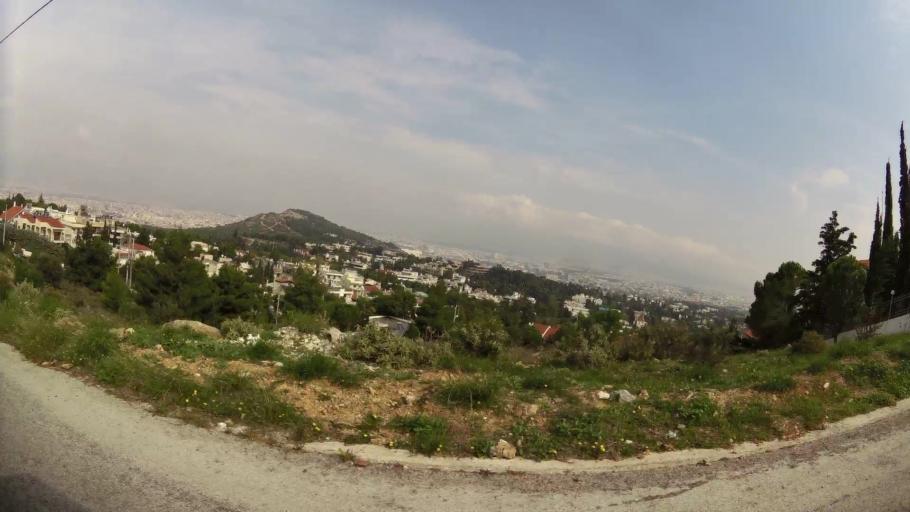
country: GR
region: Attica
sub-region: Nomarchia Athinas
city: Psychiko
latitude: 38.0143
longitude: 23.7639
